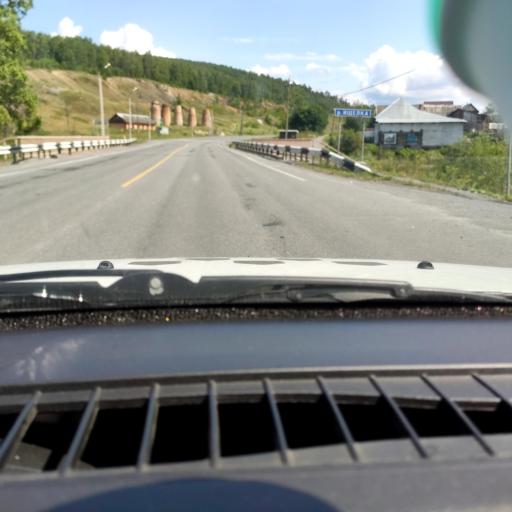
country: RU
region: Chelyabinsk
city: Mezhevoy
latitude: 55.1564
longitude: 58.8255
